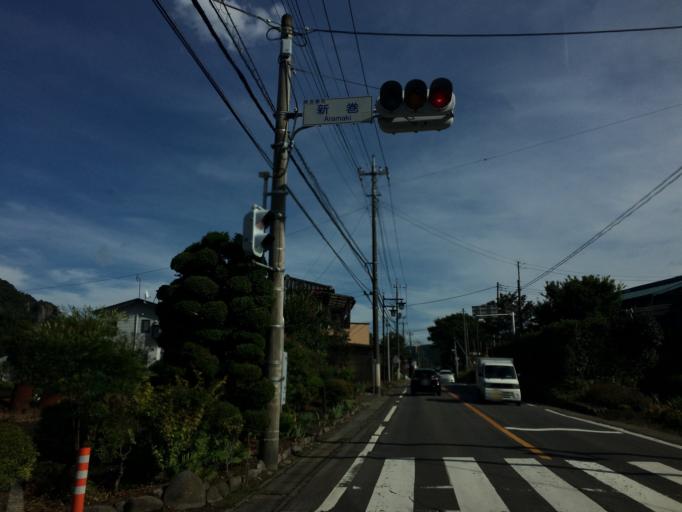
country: JP
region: Gunma
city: Nakanojomachi
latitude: 36.5626
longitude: 138.8889
